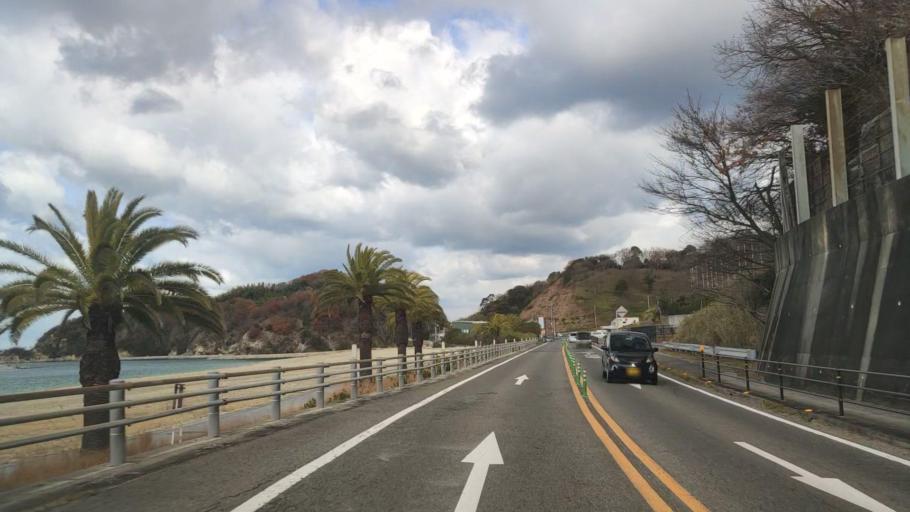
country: JP
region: Ehime
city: Hojo
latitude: 33.9939
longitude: 132.7727
